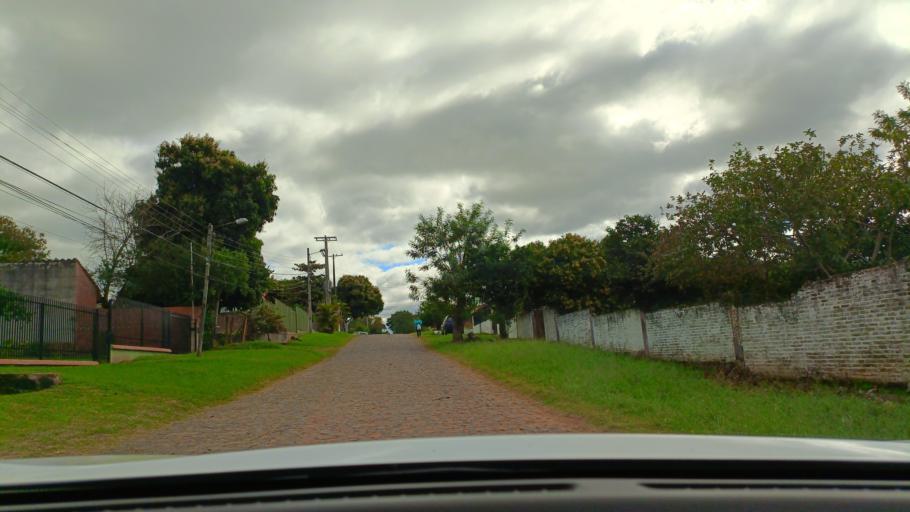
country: PY
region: San Pedro
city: Guayaybi
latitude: -24.6690
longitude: -56.4375
